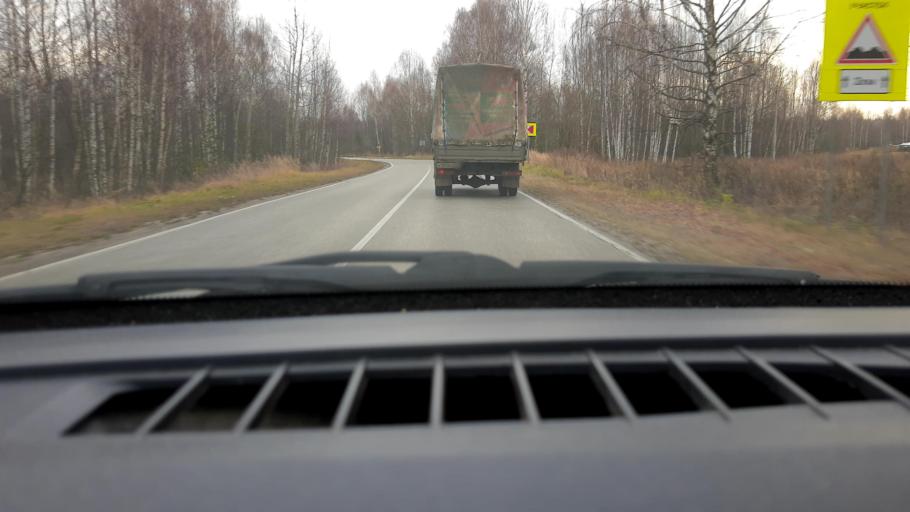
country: RU
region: Nizjnij Novgorod
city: Neklyudovo
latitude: 56.5011
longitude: 43.8507
